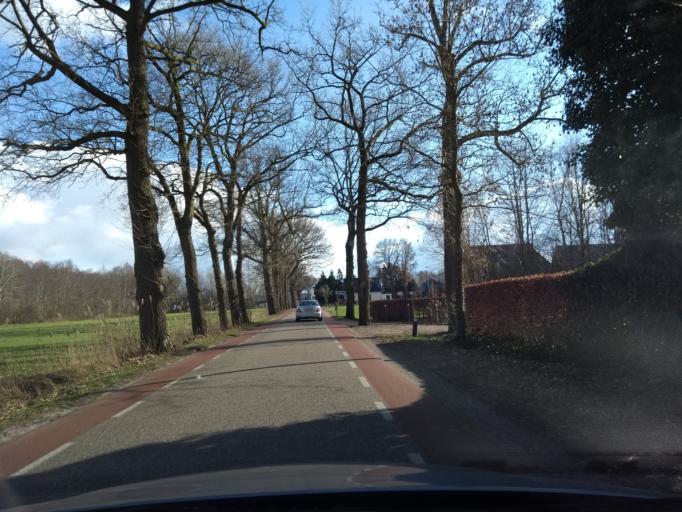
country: NL
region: Drenthe
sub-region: Gemeente De Wolden
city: Ruinen
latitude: 52.7216
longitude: 6.2997
